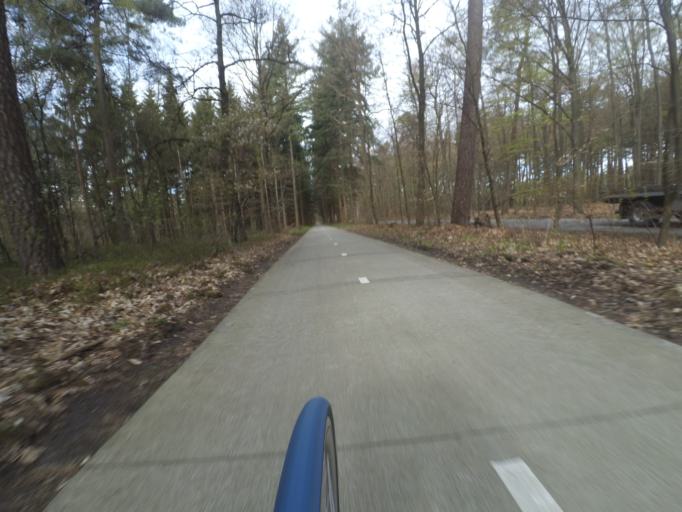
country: NL
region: Gelderland
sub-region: Gemeente Nunspeet
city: Nunspeet
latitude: 52.3369
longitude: 5.8046
